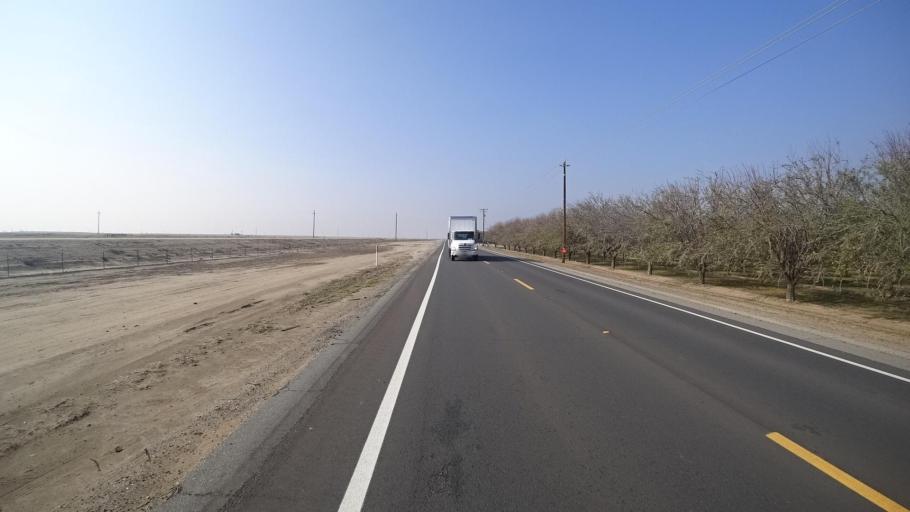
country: US
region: California
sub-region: Kern County
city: Rosedale
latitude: 35.3545
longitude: -119.2773
